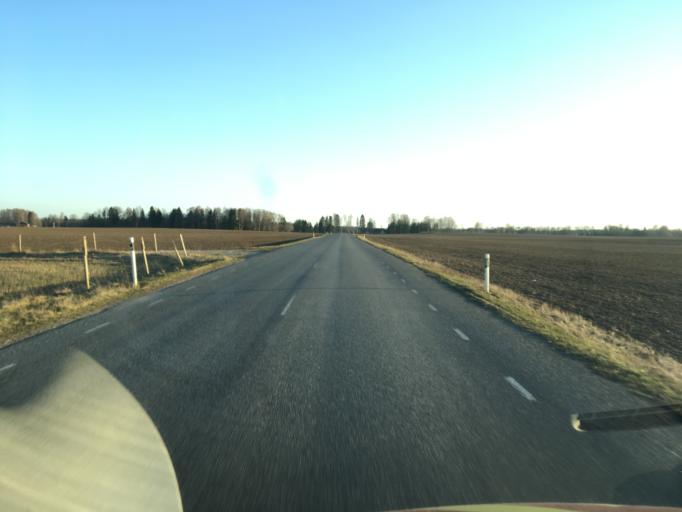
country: EE
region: Raplamaa
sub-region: Kehtna vald
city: Kehtna
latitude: 59.0184
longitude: 24.9239
